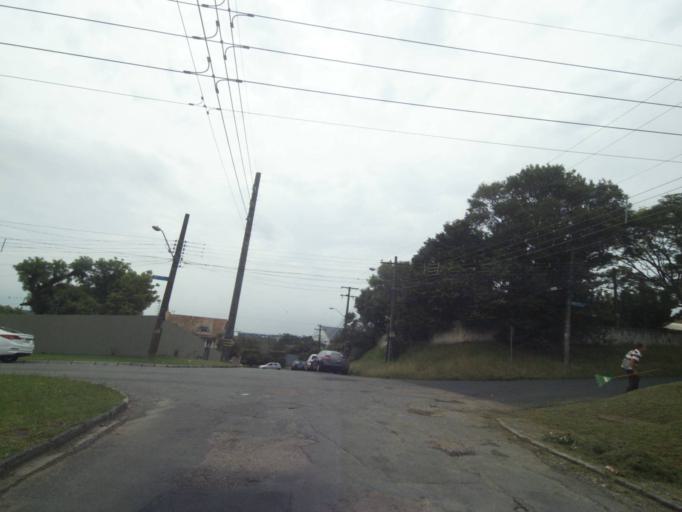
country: BR
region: Parana
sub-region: Curitiba
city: Curitiba
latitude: -25.4127
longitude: -49.2933
